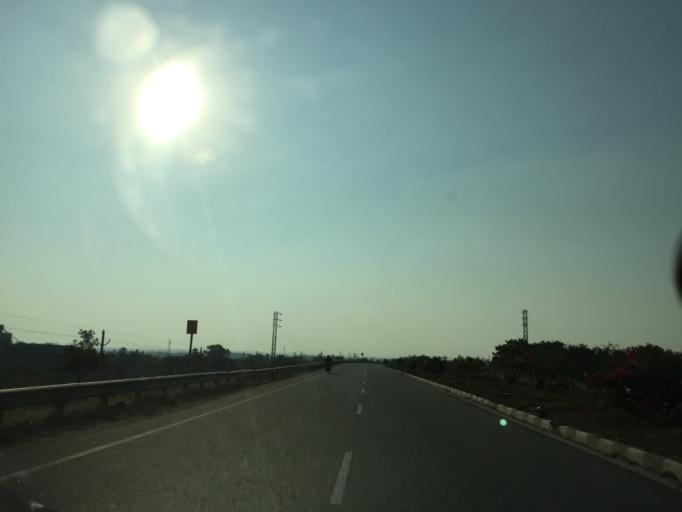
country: IN
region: Telangana
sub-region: Nalgonda
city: Bhongir
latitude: 17.5032
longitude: 78.8554
